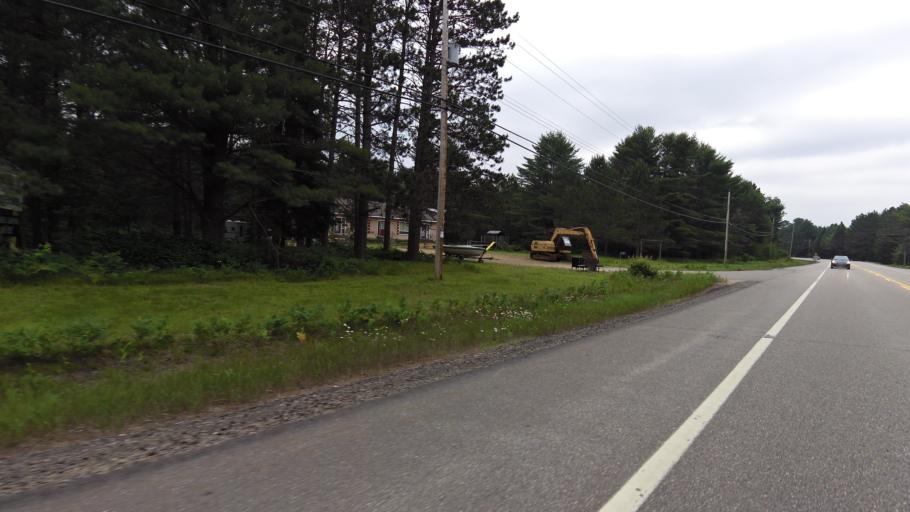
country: CA
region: Ontario
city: Huntsville
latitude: 45.3227
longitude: -78.9847
